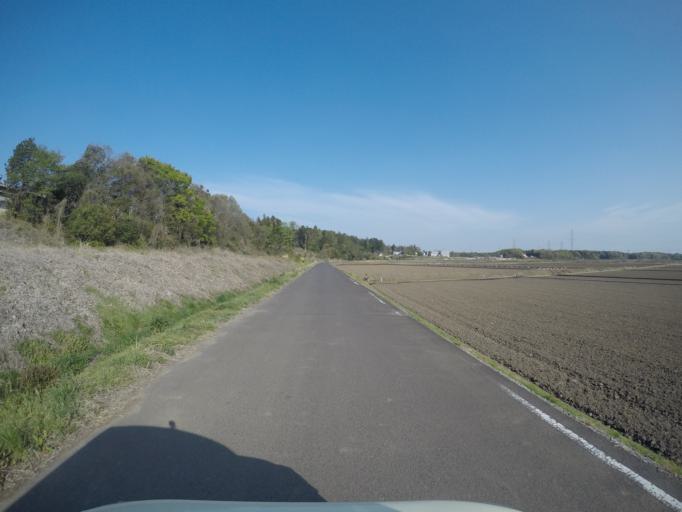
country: JP
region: Ibaraki
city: Ishige
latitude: 36.1849
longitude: 140.0138
